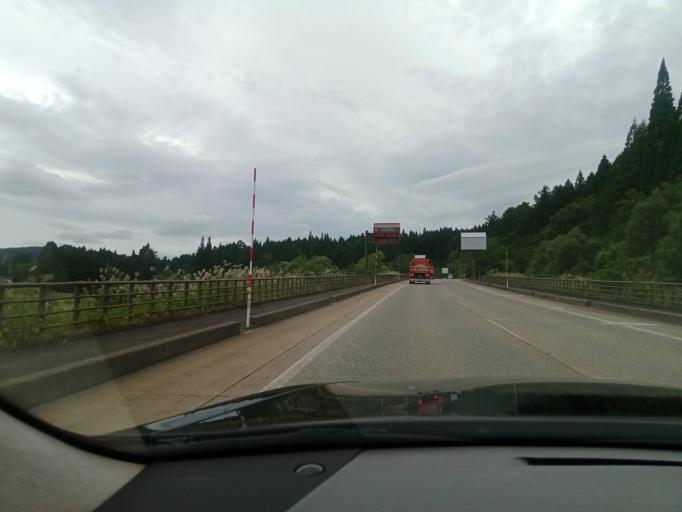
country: JP
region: Niigata
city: Arai
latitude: 36.8763
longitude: 138.2034
